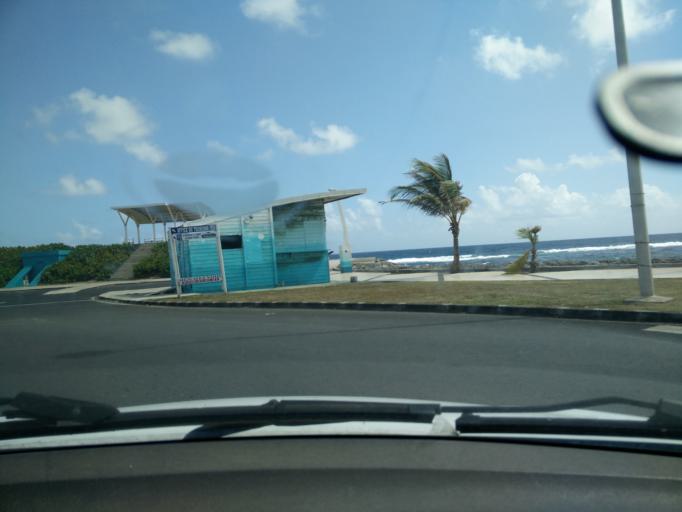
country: GP
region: Guadeloupe
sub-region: Guadeloupe
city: Le Moule
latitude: 16.3349
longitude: -61.3570
